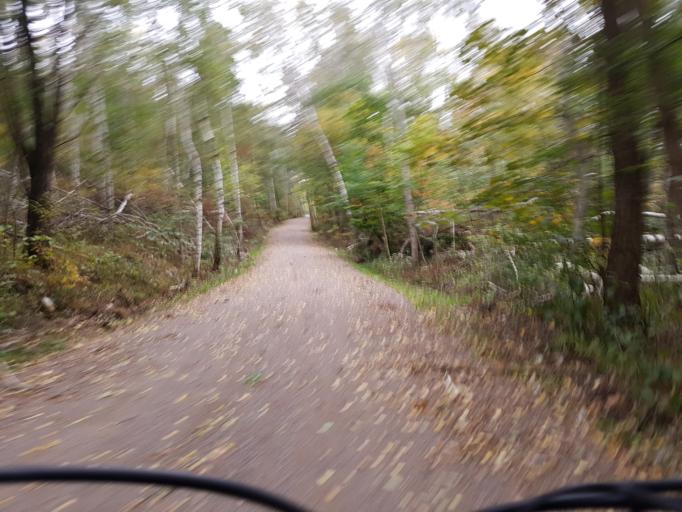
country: DE
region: Brandenburg
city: Trobitz
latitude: 51.5858
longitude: 13.4204
